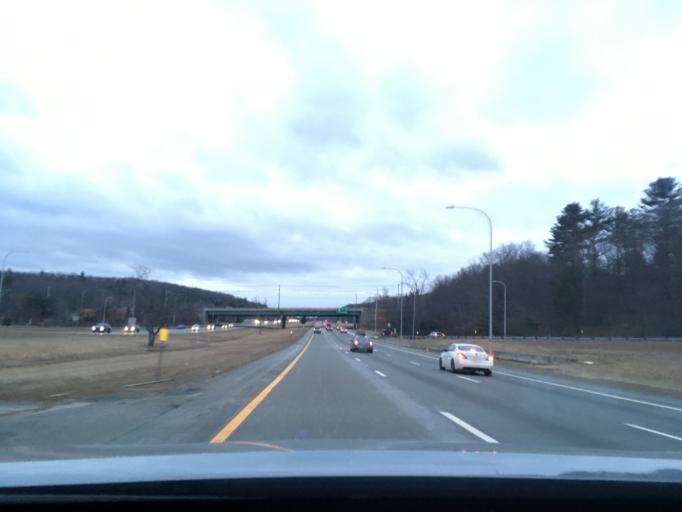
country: US
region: Rhode Island
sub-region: Providence County
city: Greenville
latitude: 41.8724
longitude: -71.5154
